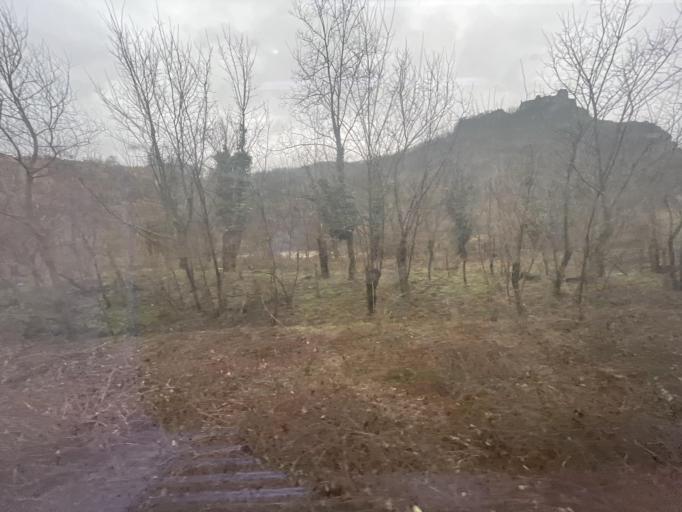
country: GE
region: Imereti
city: Kharagauli
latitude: 42.0006
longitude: 43.2246
